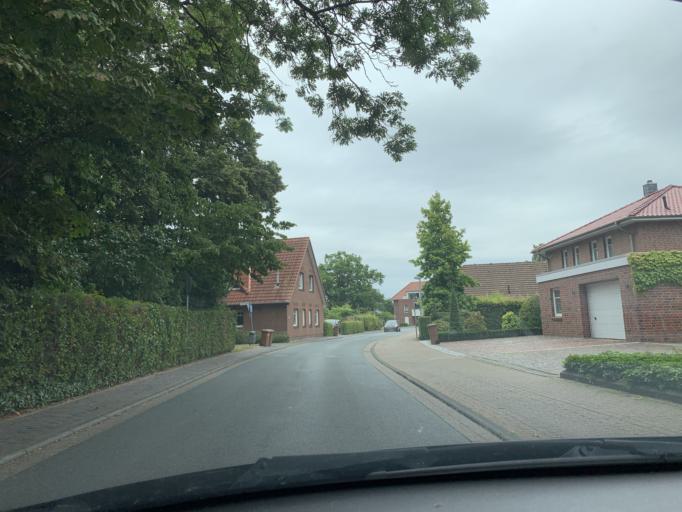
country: DE
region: Lower Saxony
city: Westerstede
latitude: 53.2547
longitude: 7.9233
